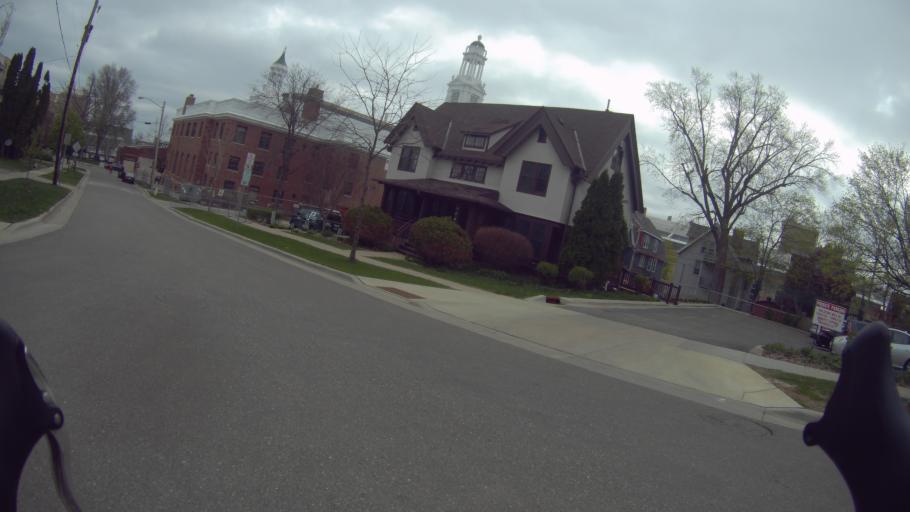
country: US
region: Wisconsin
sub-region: Dane County
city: Madison
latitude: 43.0726
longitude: -89.4151
